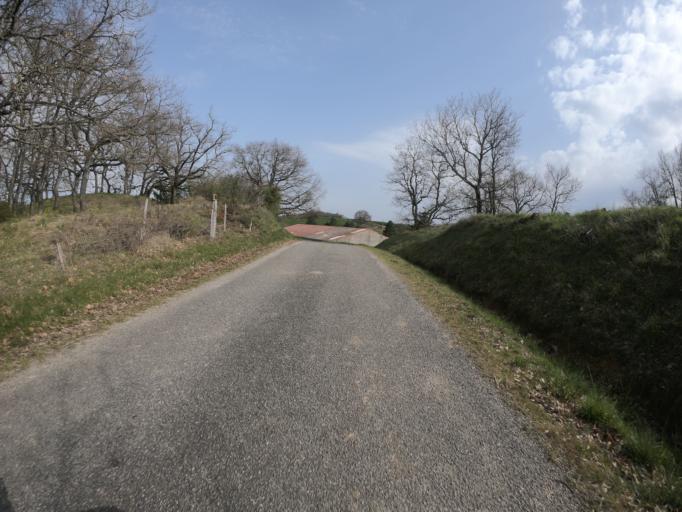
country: FR
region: Languedoc-Roussillon
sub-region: Departement de l'Aude
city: Belpech
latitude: 43.1550
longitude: 1.7773
